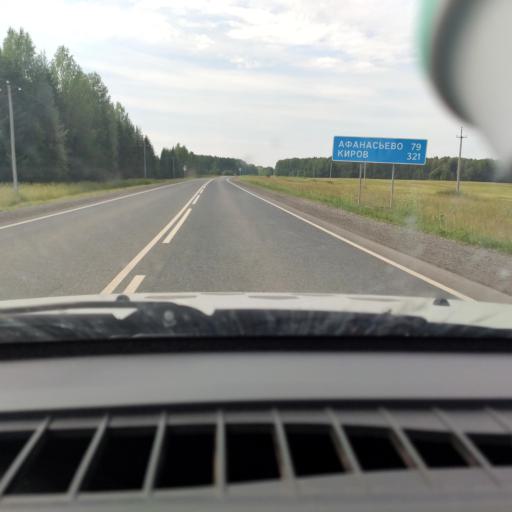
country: RU
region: Perm
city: Siva
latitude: 58.4864
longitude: 54.0667
